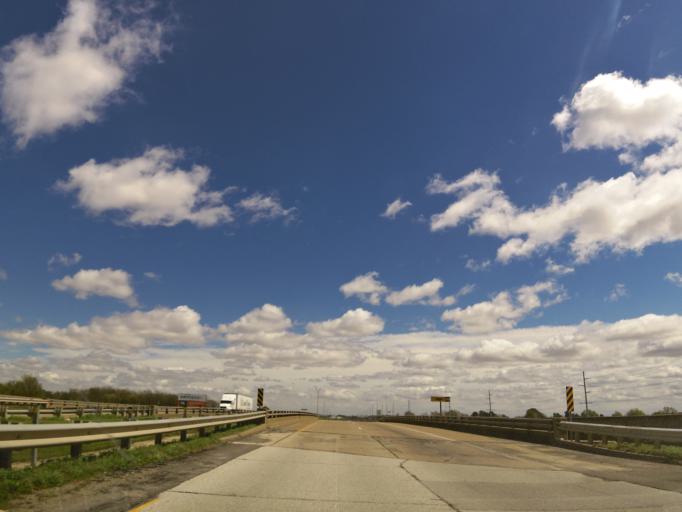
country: US
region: Arkansas
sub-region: Craighead County
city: Jonesboro
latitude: 35.8070
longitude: -90.6589
